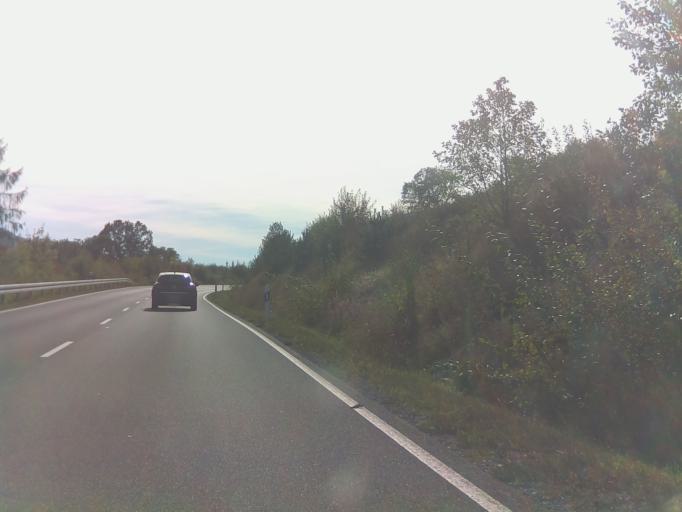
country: DE
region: Hesse
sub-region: Regierungsbezirk Kassel
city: Hilders
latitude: 50.5440
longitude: 9.9890
